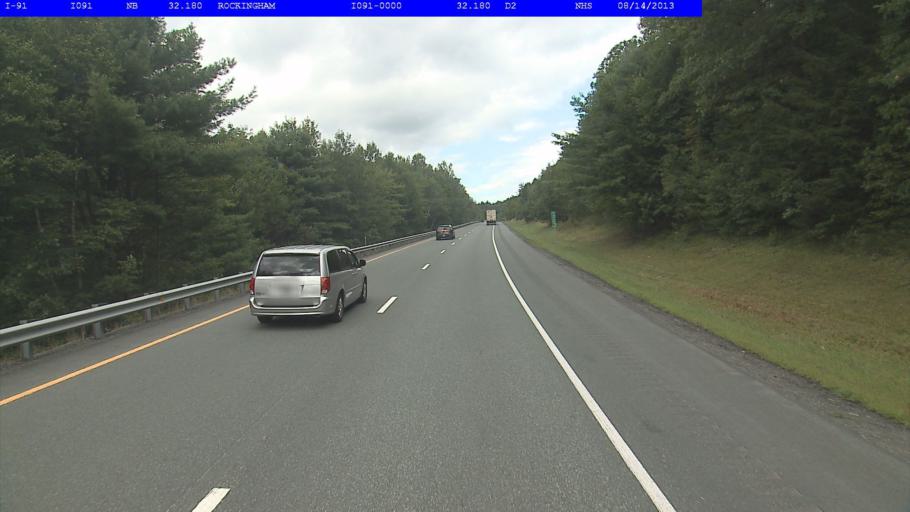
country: US
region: Vermont
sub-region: Windham County
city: Bellows Falls
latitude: 43.1380
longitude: -72.4761
